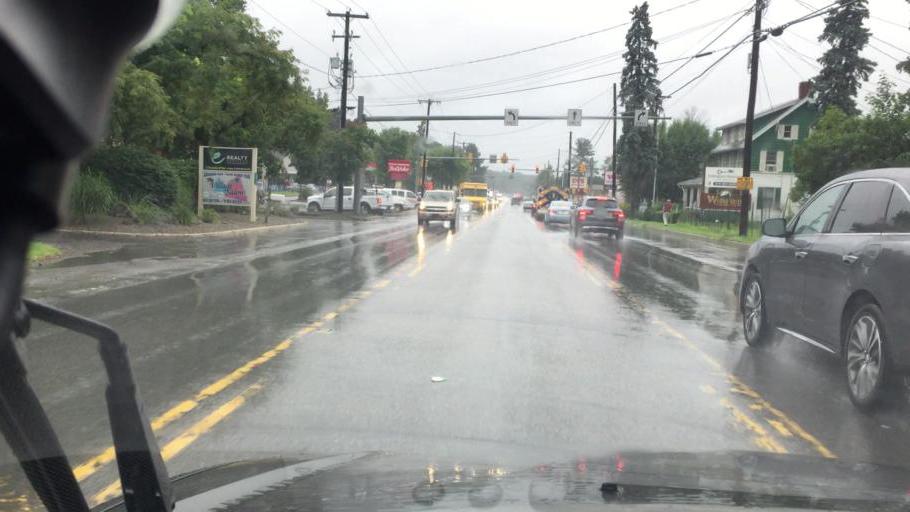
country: US
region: Pennsylvania
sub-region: Monroe County
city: Tannersville
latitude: 41.0419
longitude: -75.3072
